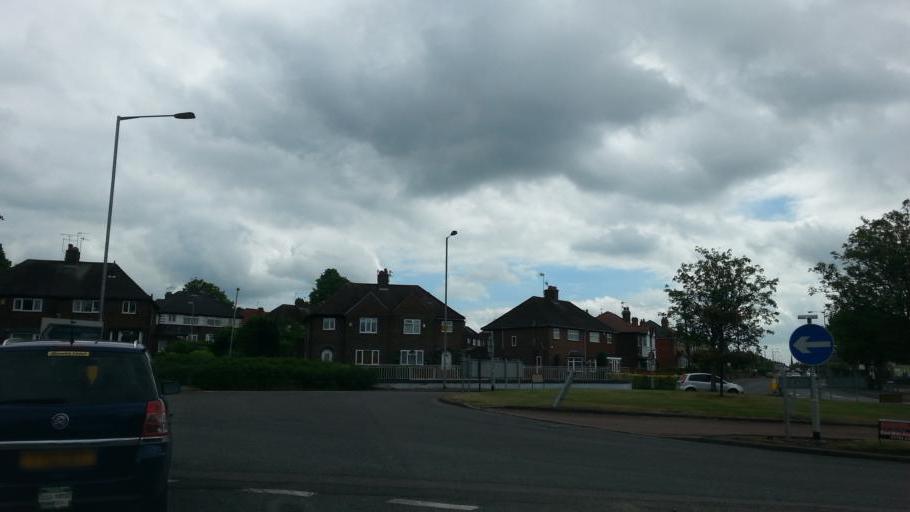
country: GB
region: England
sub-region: Staffordshire
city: Newcastle under Lyme
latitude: 53.0362
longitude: -2.2397
